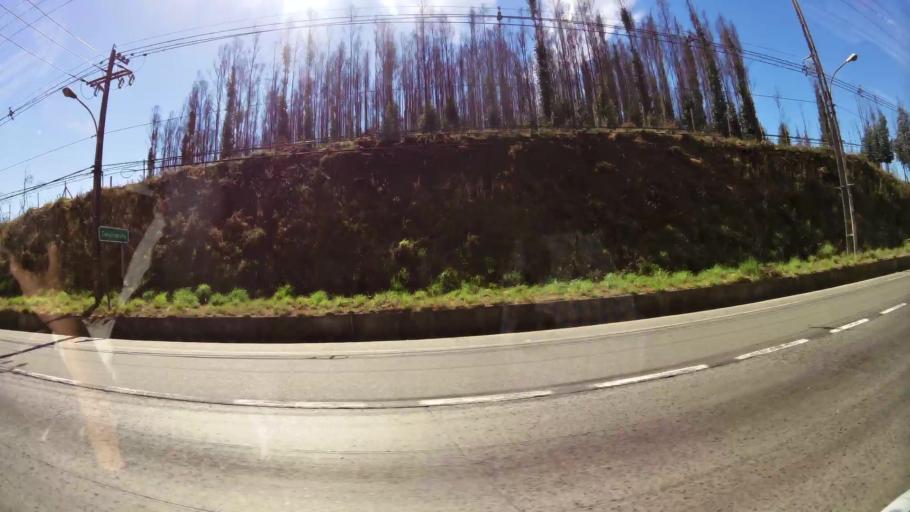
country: CL
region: Biobio
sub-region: Provincia de Concepcion
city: Penco
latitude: -36.7569
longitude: -73.0031
